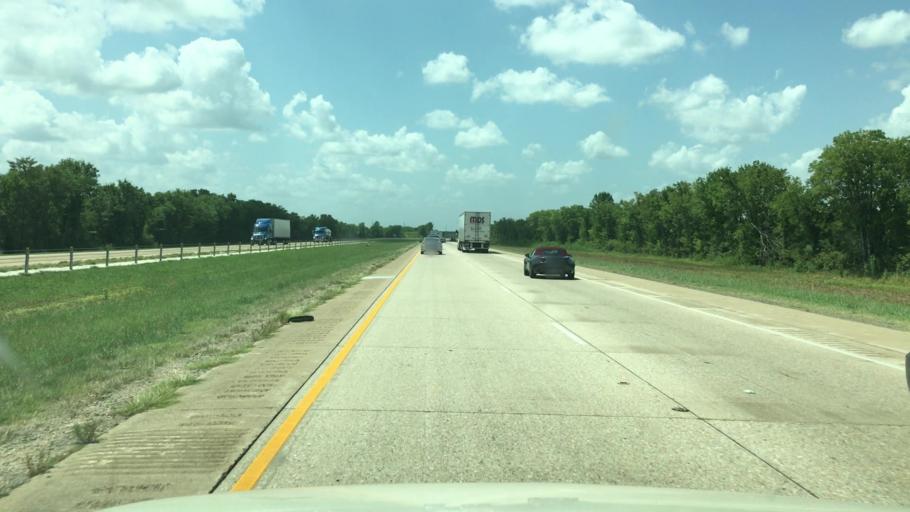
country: US
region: Arkansas
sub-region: Miller County
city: Texarkana
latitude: 33.5807
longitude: -93.8435
